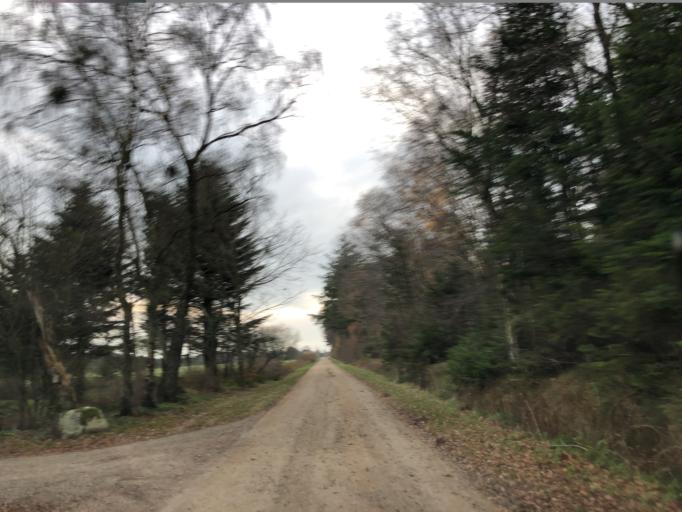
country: DK
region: Central Jutland
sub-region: Holstebro Kommune
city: Ulfborg
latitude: 56.2854
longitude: 8.1842
